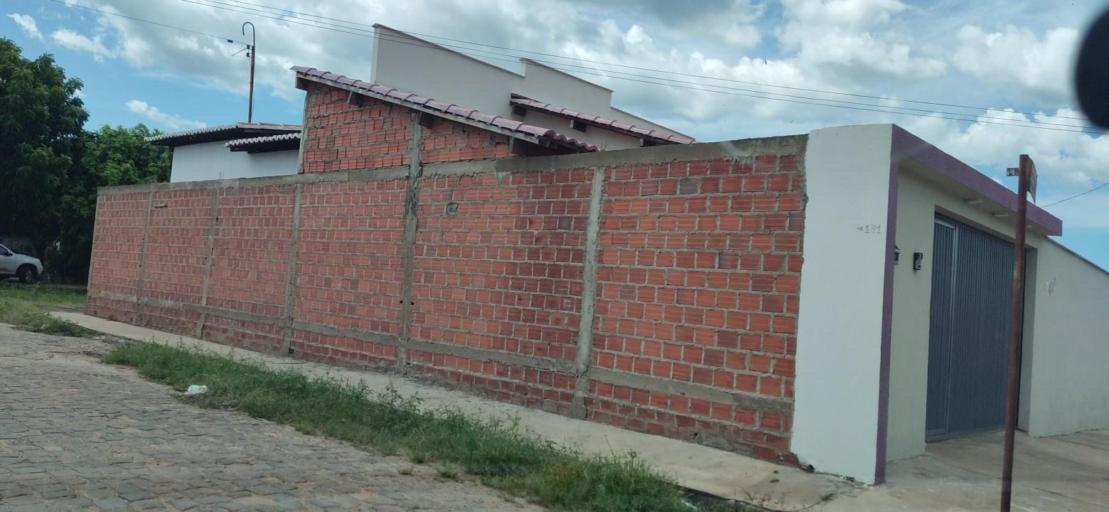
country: BR
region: Piaui
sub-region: Valenca Do Piaui
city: Valenca do Piaui
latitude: -6.4022
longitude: -41.7330
